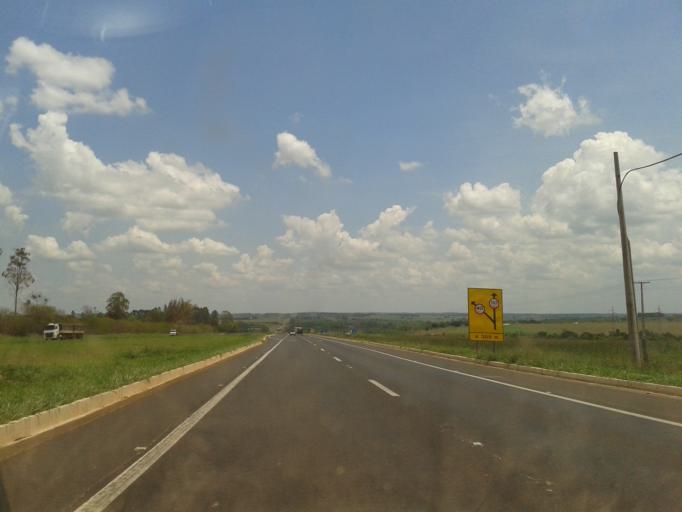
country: BR
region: Minas Gerais
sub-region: Uberlandia
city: Uberlandia
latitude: -18.8918
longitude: -48.4210
